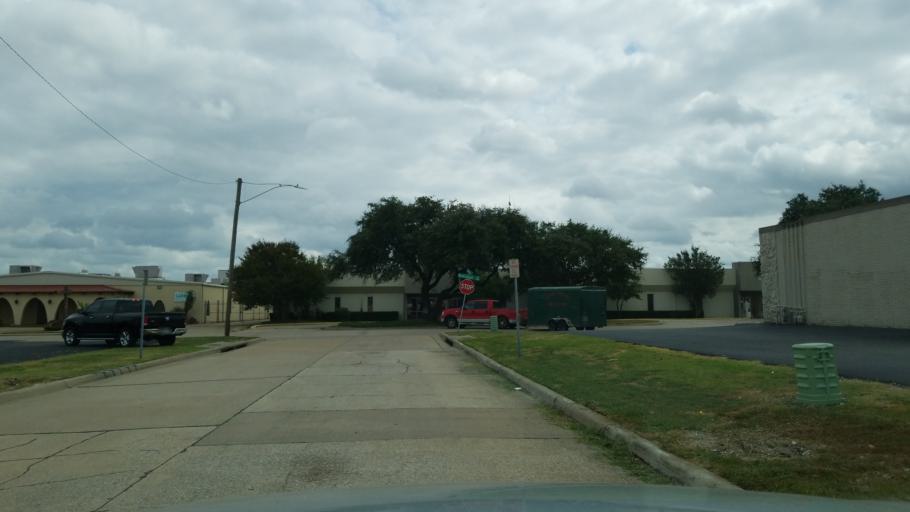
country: US
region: Texas
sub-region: Dallas County
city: Garland
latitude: 32.8820
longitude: -96.6731
